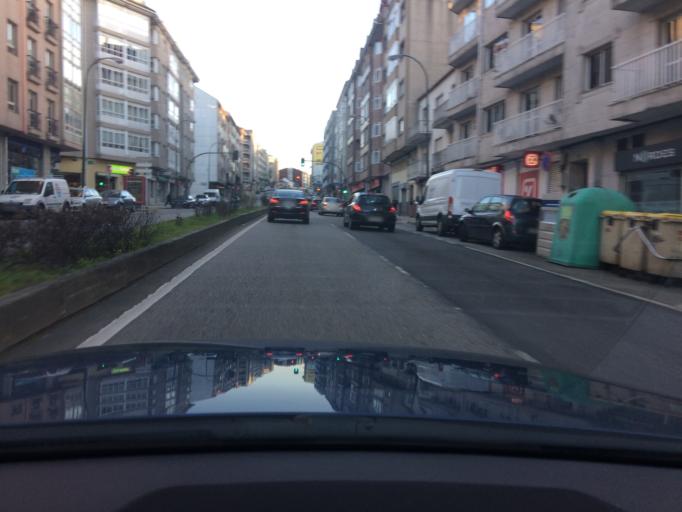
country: ES
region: Galicia
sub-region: Provincia da Coruna
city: Santiago de Compostela
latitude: 42.8463
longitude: -8.5755
